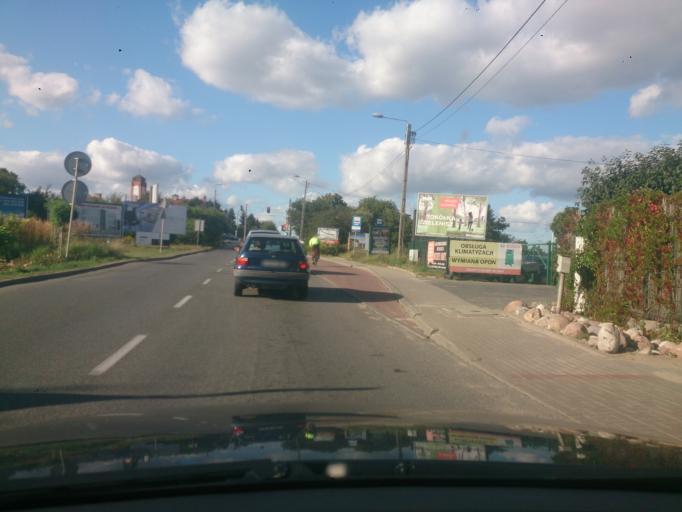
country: PL
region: Pomeranian Voivodeship
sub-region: Gdynia
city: Wielki Kack
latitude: 54.4675
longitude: 18.5093
